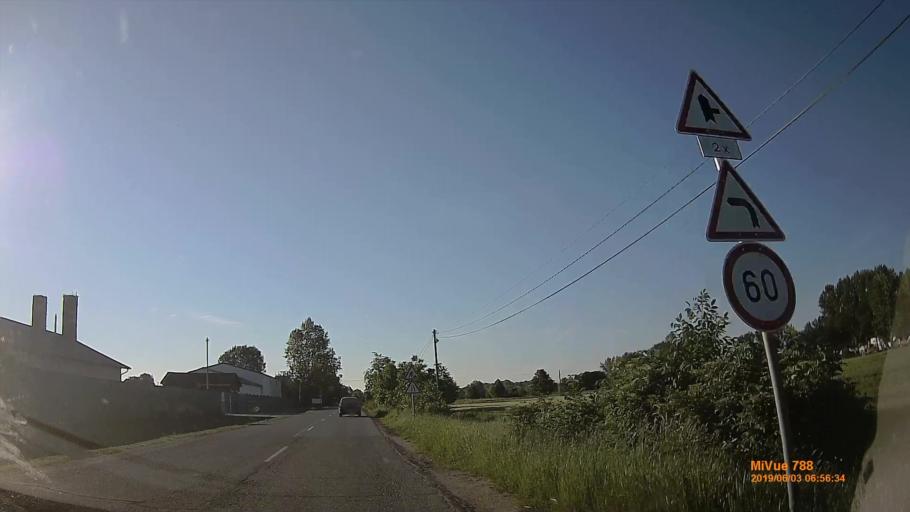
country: HU
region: Pest
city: Dabas
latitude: 47.2158
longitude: 19.2610
